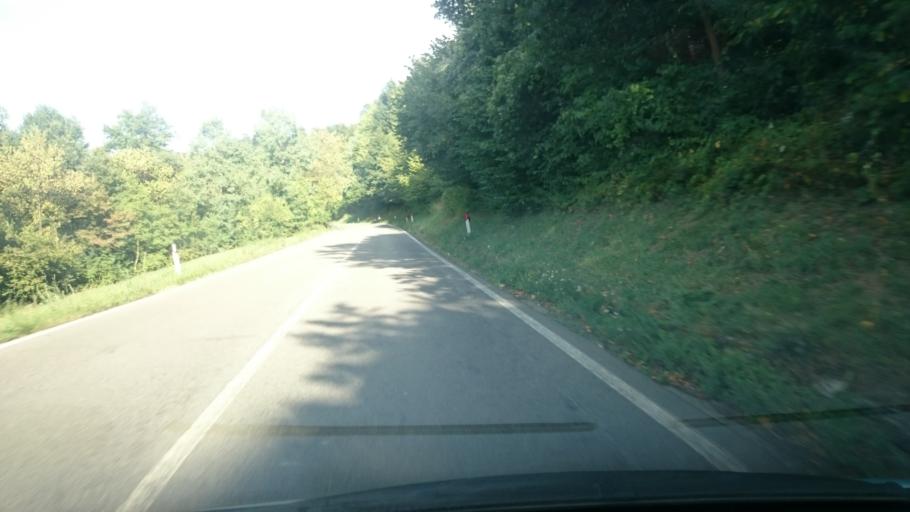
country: IT
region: Emilia-Romagna
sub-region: Provincia di Reggio Emilia
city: Carpineti
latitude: 44.4060
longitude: 10.5175
